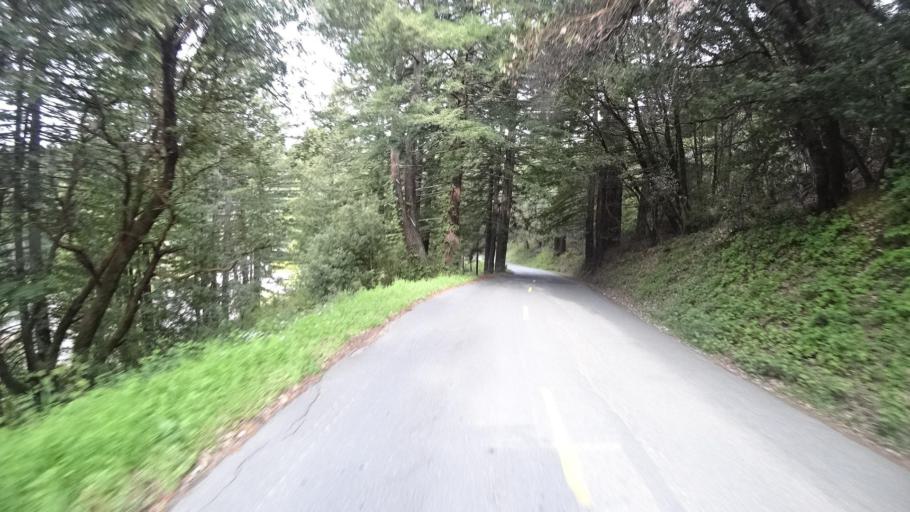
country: US
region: California
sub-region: Humboldt County
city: Redway
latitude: 40.2940
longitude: -123.8347
